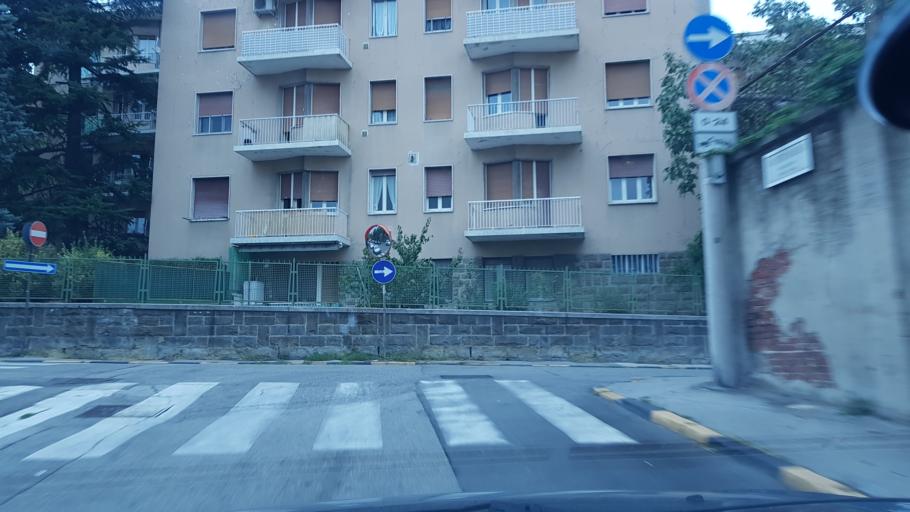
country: IT
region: Friuli Venezia Giulia
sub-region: Provincia di Trieste
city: Trieste
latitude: 45.6229
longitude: 13.8007
